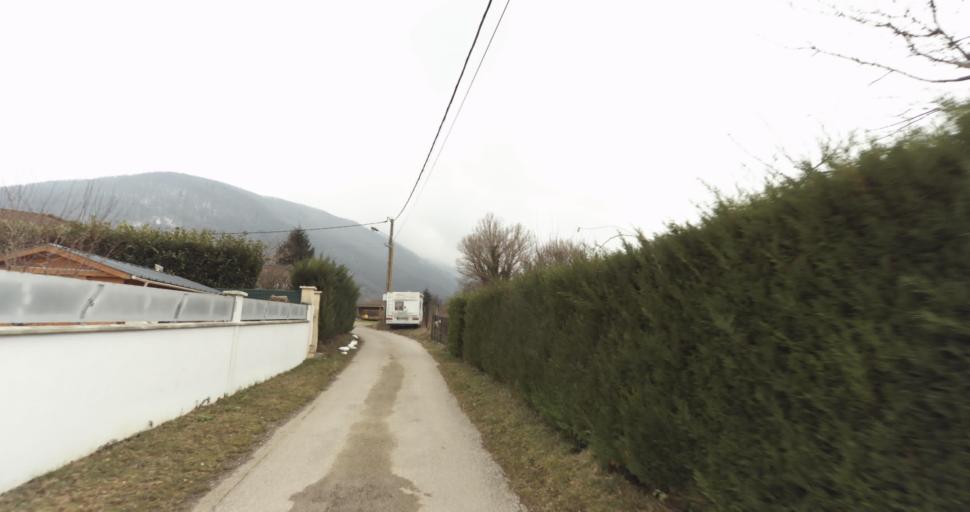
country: FR
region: Rhone-Alpes
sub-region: Departement de l'Isere
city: Le Gua
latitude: 45.0214
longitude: 5.6544
